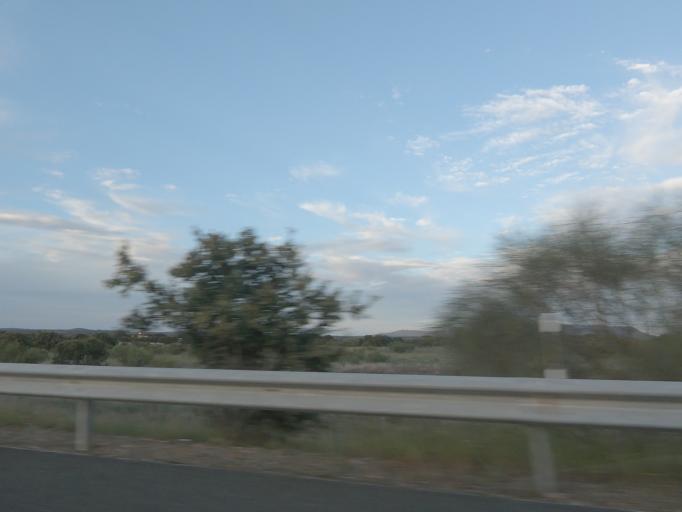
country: ES
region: Extremadura
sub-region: Provincia de Caceres
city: Casas de Don Antonio
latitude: 39.1922
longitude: -6.2774
